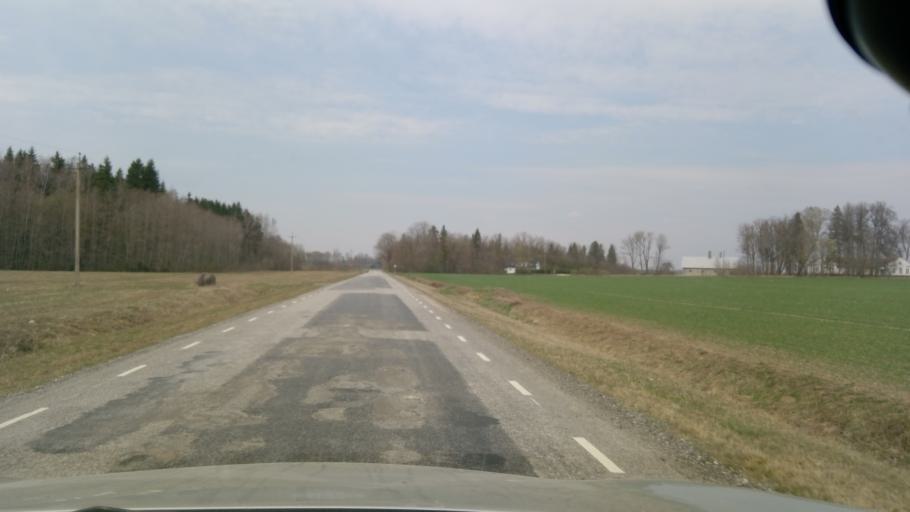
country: EE
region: Jaervamaa
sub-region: Tueri vald
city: Tueri
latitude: 58.8015
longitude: 25.4745
